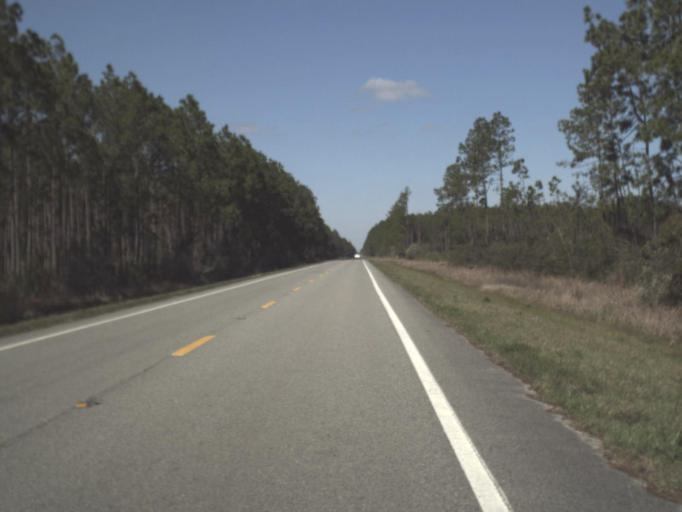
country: US
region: Florida
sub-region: Gulf County
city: Port Saint Joe
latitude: 29.9219
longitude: -85.1984
